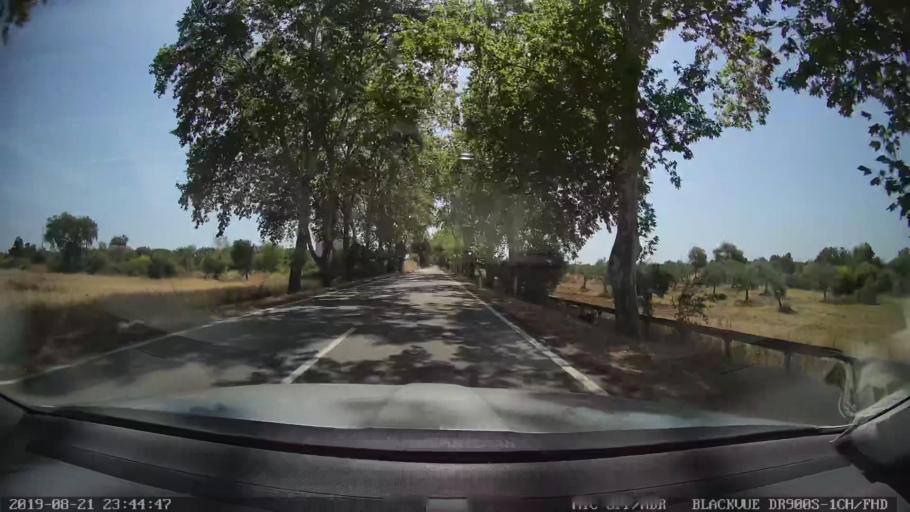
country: PT
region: Castelo Branco
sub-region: Idanha-A-Nova
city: Idanha-a-Nova
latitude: 39.8447
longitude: -7.2739
